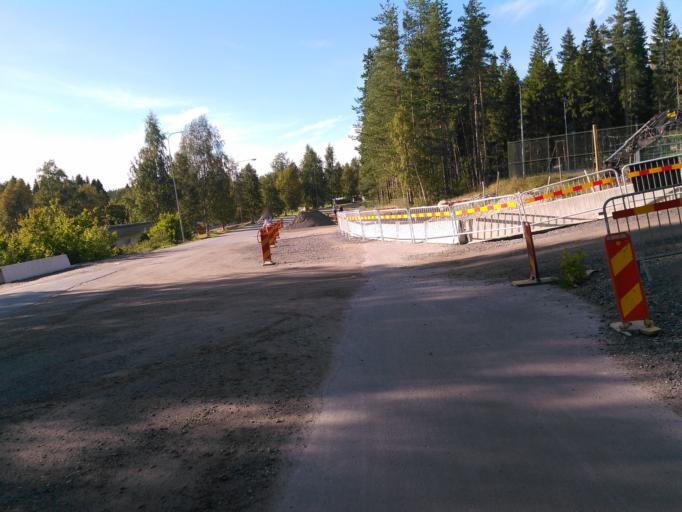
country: SE
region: Vaesterbotten
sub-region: Umea Kommun
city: Ersmark
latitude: 63.8288
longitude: 20.3242
